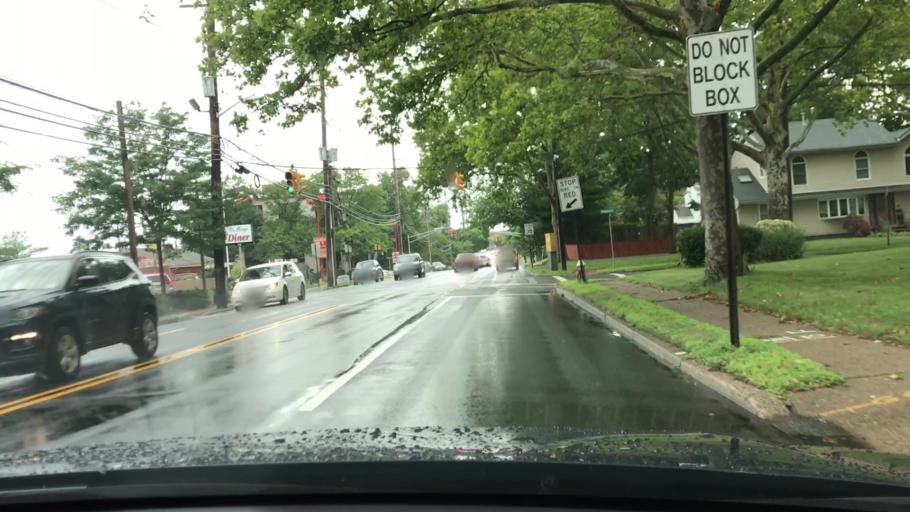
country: US
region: New Jersey
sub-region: Bergen County
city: Paramus
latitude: 40.9664
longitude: -74.0707
